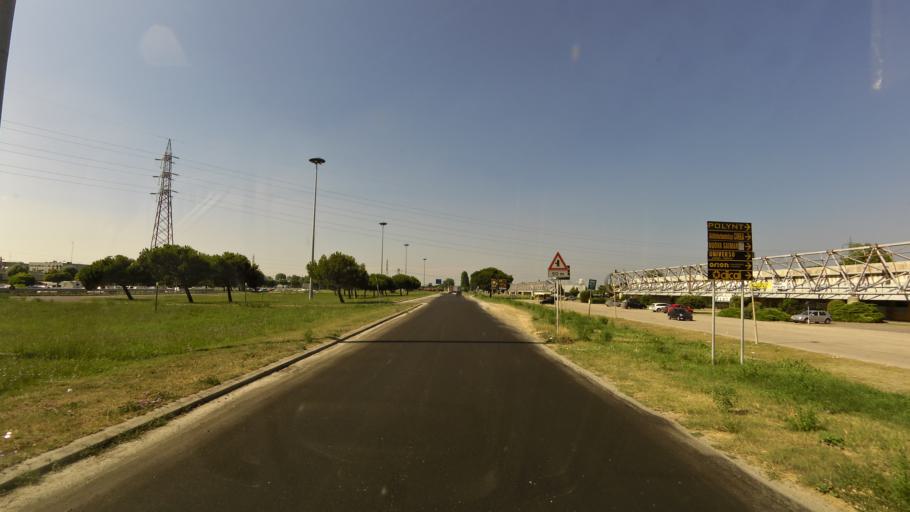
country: IT
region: Emilia-Romagna
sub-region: Provincia di Ravenna
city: Ravenna
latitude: 44.4466
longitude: 12.2103
